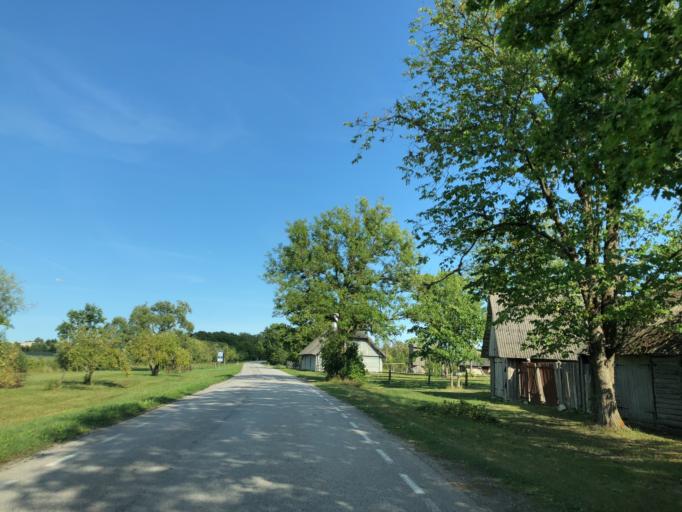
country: EE
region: Hiiumaa
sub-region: Kaerdla linn
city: Kardla
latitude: 58.8248
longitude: 22.7601
